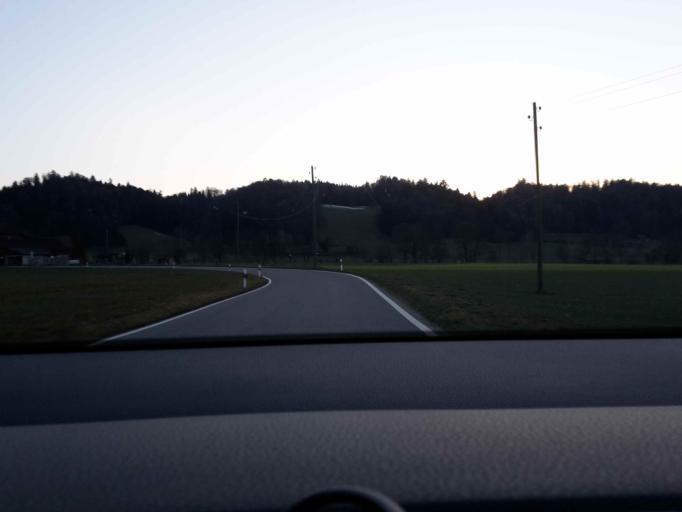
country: CH
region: Bern
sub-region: Oberaargau
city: Rohrbach
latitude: 47.1330
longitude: 7.8094
